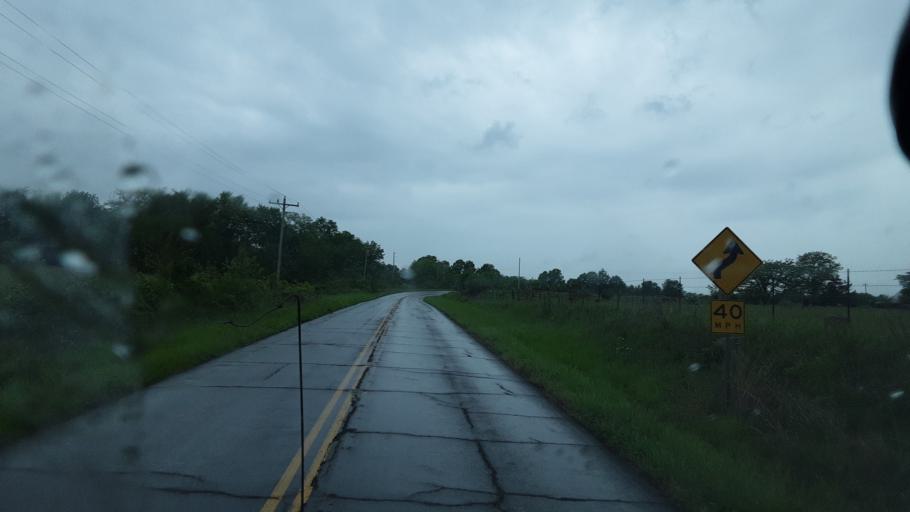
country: US
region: Missouri
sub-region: Boone County
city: Centralia
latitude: 39.3888
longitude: -92.2314
